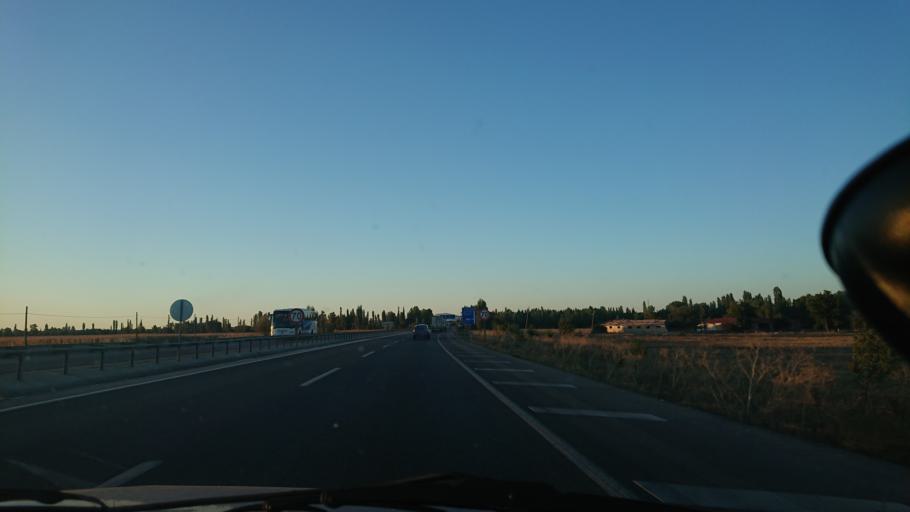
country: TR
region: Eskisehir
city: Mahmudiye
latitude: 39.5645
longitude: 30.9148
